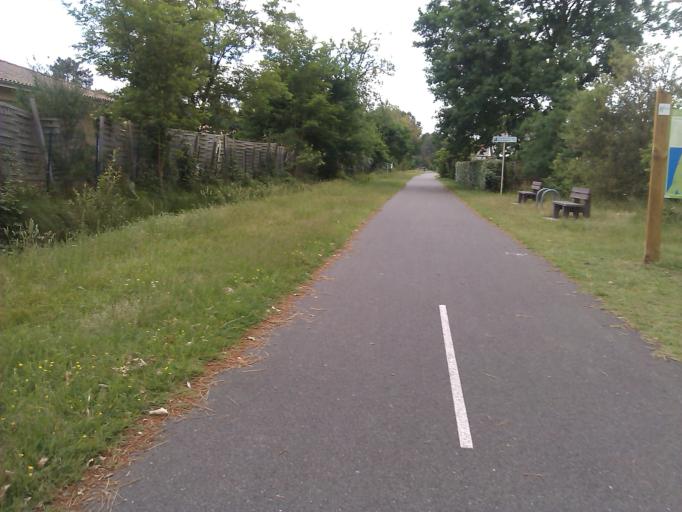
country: FR
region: Aquitaine
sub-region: Departement des Landes
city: Leon
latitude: 43.8477
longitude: -1.3530
